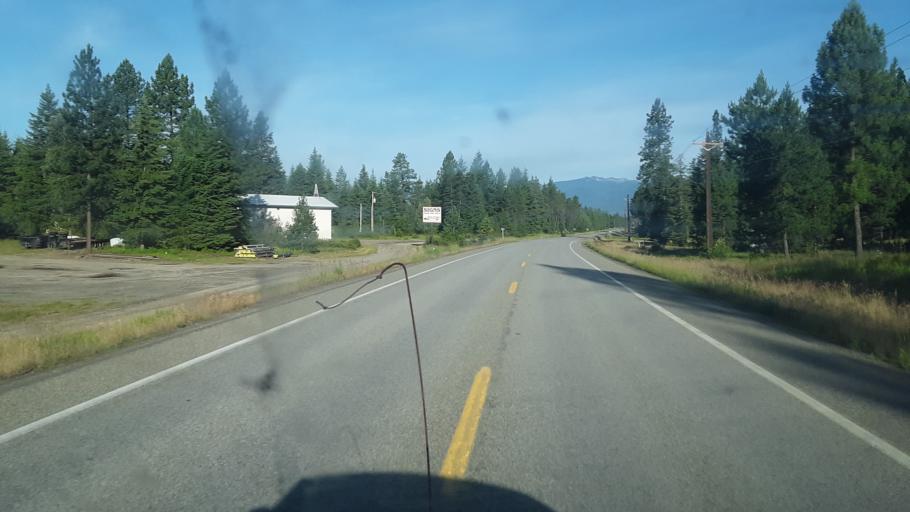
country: US
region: Idaho
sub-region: Boundary County
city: Bonners Ferry
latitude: 48.7266
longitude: -116.2104
